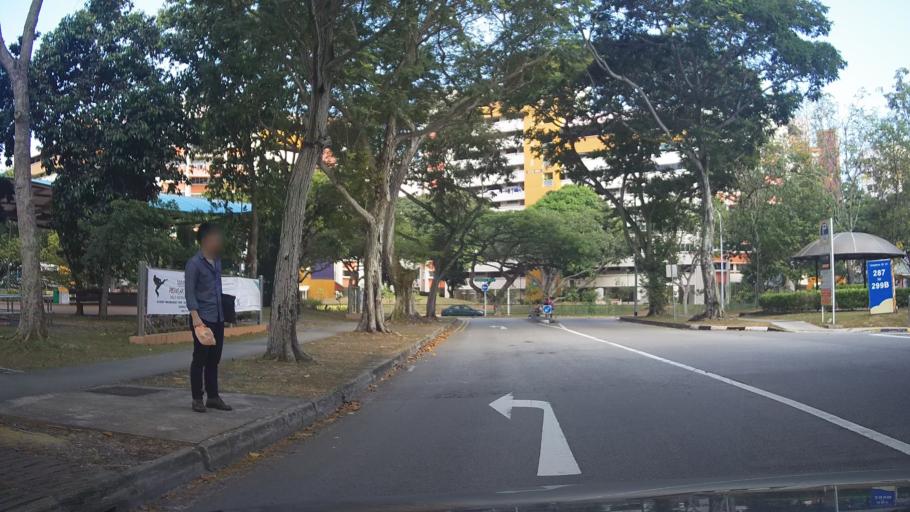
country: SG
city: Singapore
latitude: 1.3501
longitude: 103.9536
